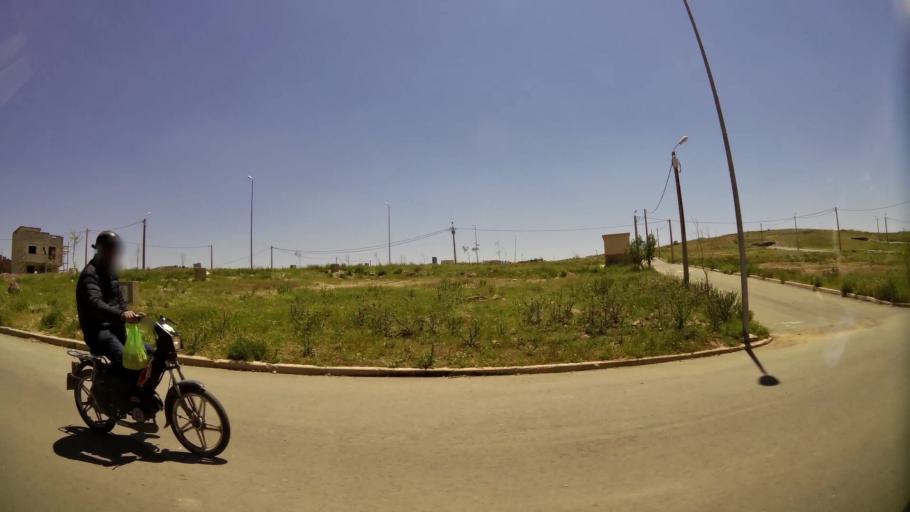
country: MA
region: Oriental
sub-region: Oujda-Angad
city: Oujda
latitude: 34.6557
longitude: -1.9256
